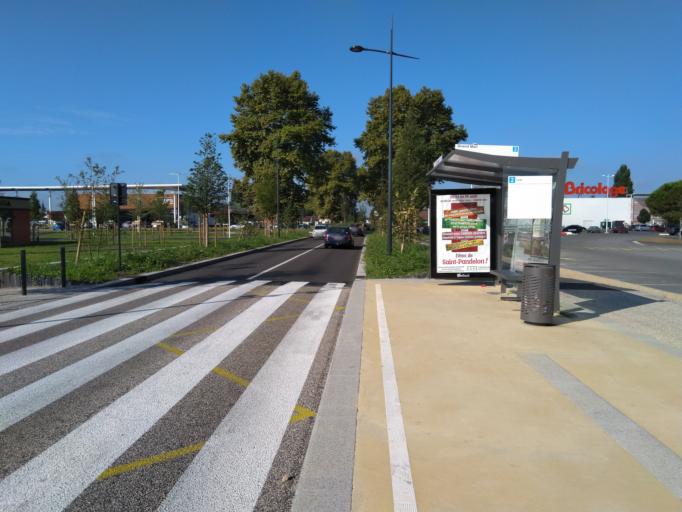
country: FR
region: Aquitaine
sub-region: Departement des Landes
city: Saint-Paul-les-Dax
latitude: 43.7292
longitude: -1.0393
